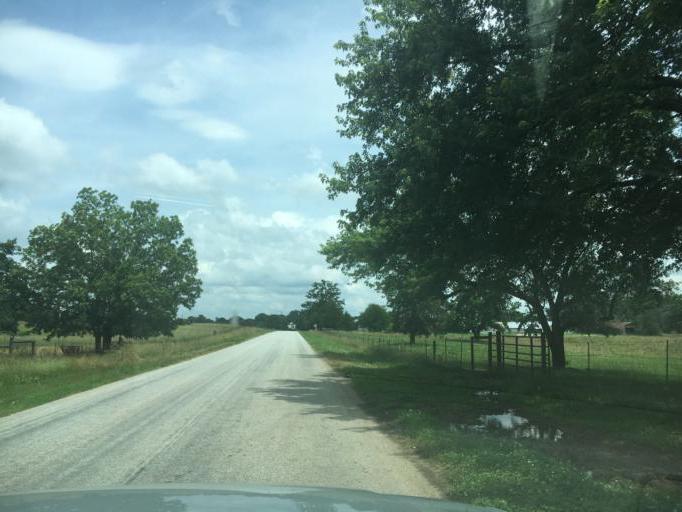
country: US
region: Georgia
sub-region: Franklin County
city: Gumlog
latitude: 34.4627
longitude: -83.0674
